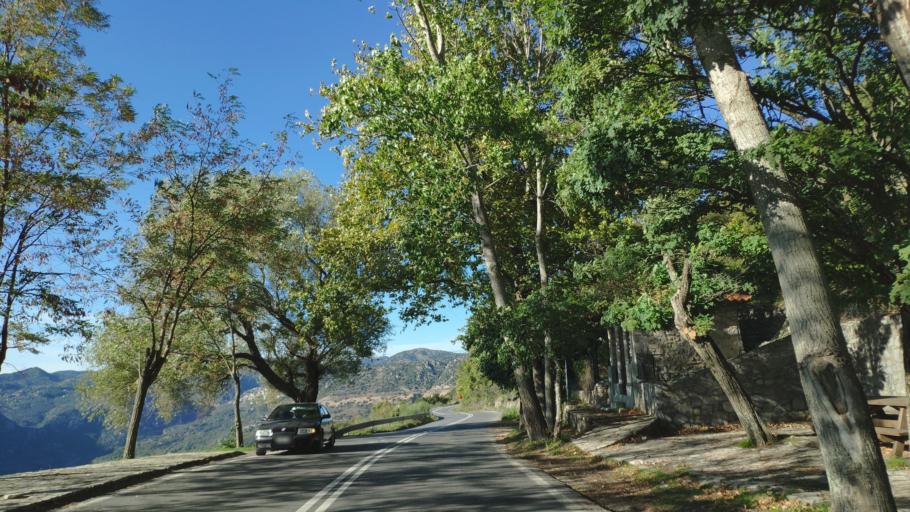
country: GR
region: Peloponnese
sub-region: Nomos Arkadias
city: Dimitsana
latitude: 37.5600
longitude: 22.0629
